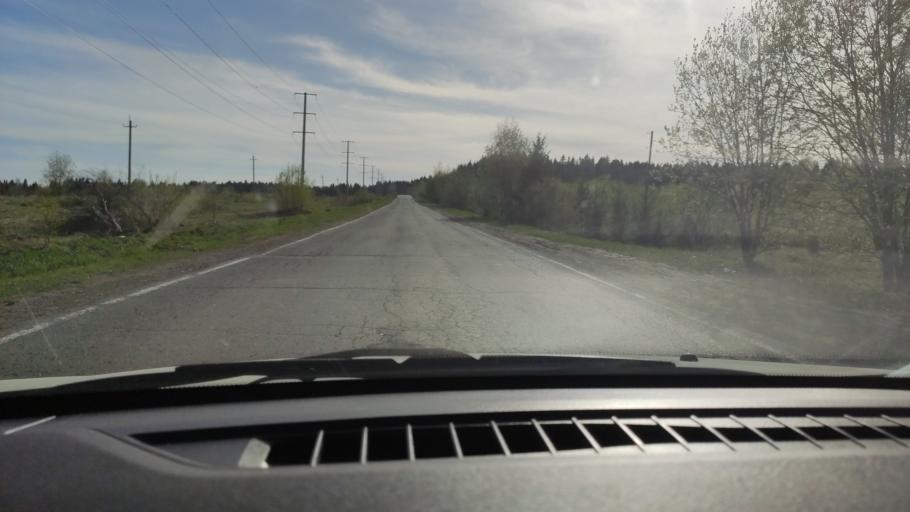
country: RU
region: Perm
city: Novyye Lyady
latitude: 57.9213
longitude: 56.6723
